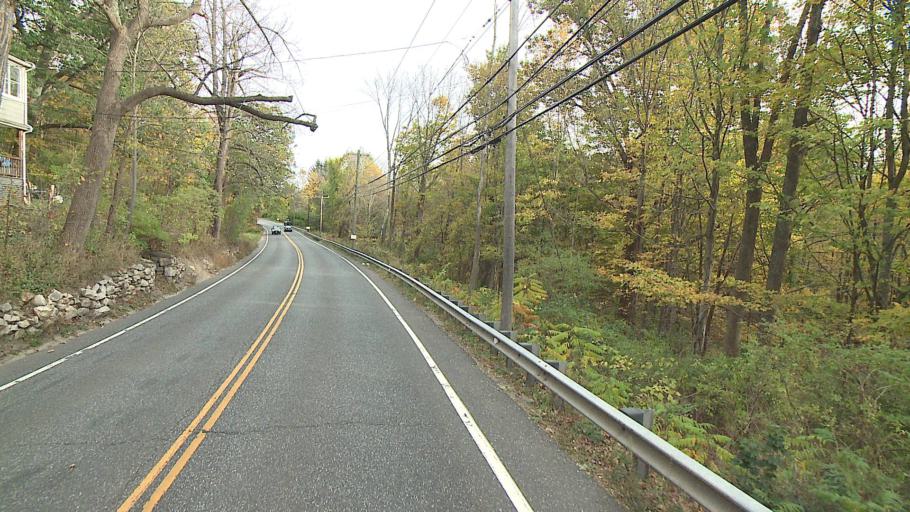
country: US
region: Connecticut
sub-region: Litchfield County
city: Canaan
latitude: 42.0156
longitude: -73.2994
